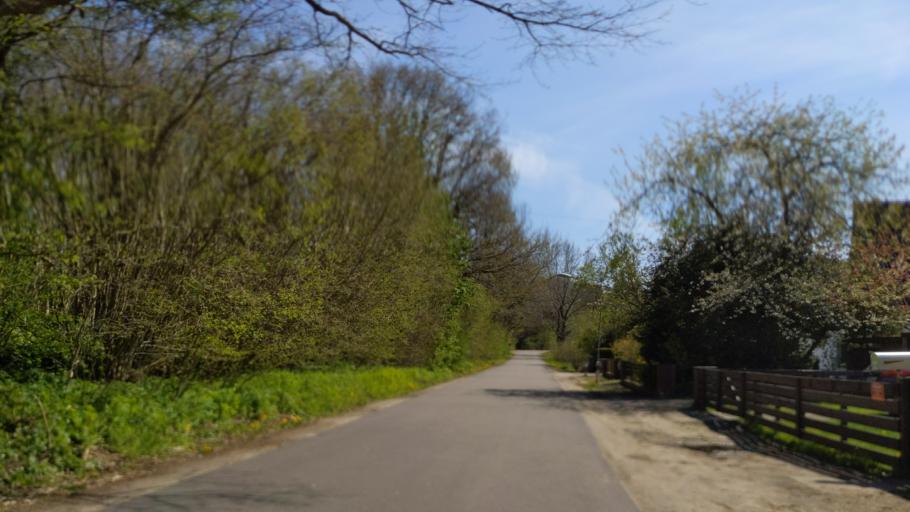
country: DE
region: Schleswig-Holstein
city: Ratekau
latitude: 53.9263
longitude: 10.7681
